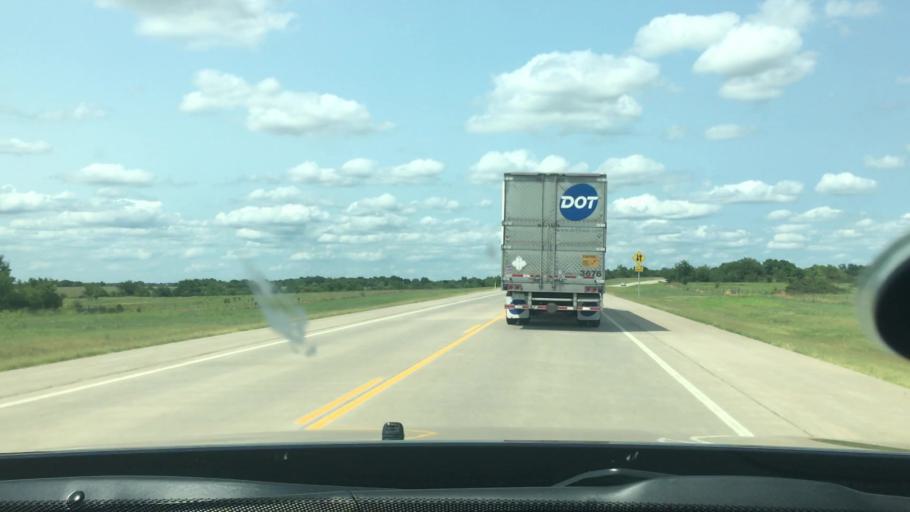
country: US
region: Oklahoma
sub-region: Murray County
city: Sulphur
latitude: 34.5743
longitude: -96.9257
